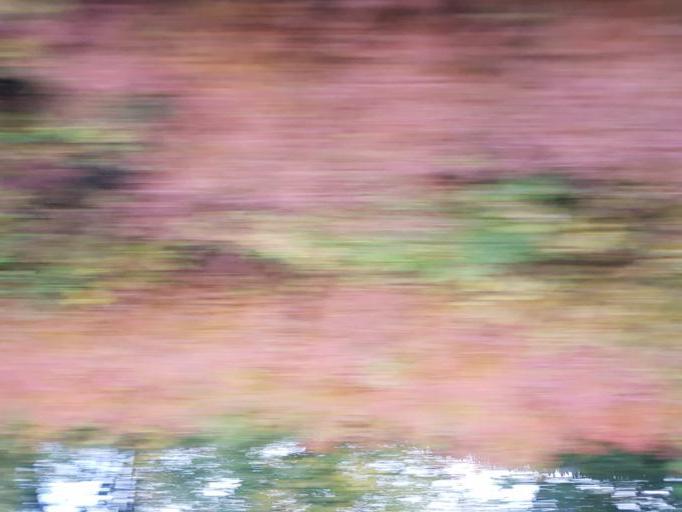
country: NO
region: Sor-Trondelag
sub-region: Melhus
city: Melhus
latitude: 63.2208
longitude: 10.2853
